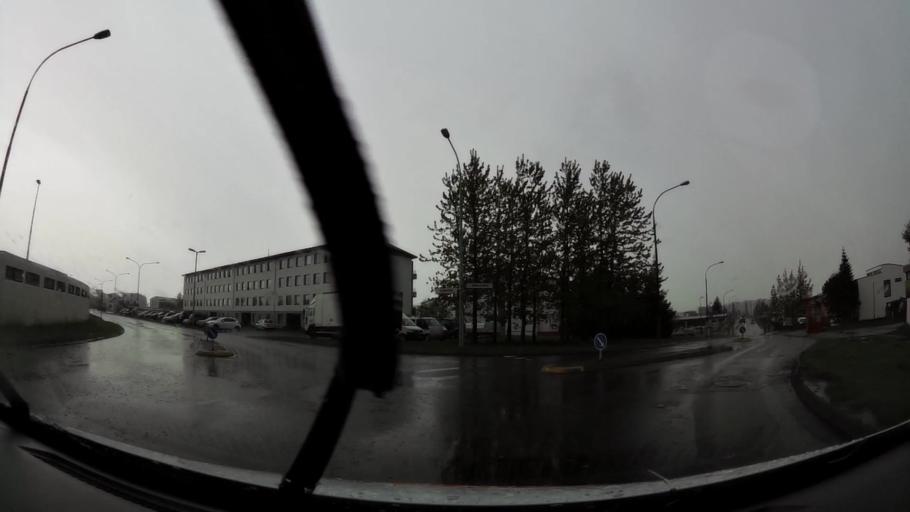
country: IS
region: Capital Region
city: Reykjavik
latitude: 64.1086
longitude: -21.8206
